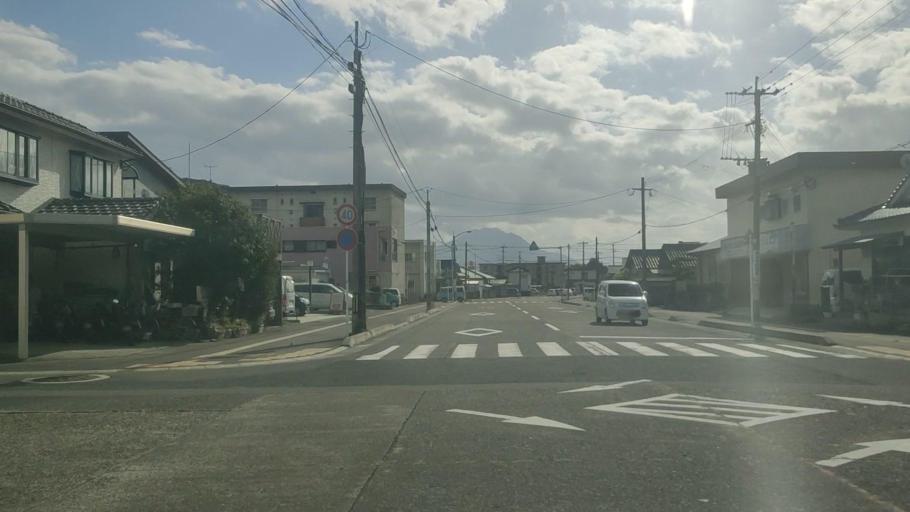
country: JP
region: Kagoshima
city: Kajiki
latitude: 31.7365
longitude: 130.6702
